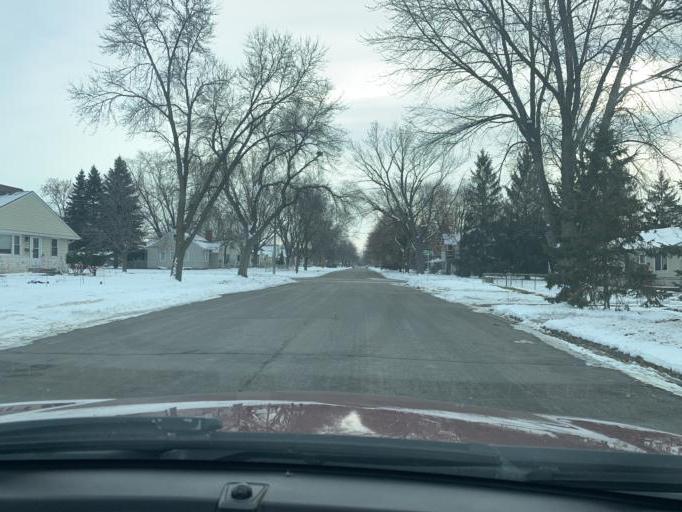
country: US
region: Minnesota
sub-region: Washington County
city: Saint Paul Park
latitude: 44.8447
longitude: -92.9886
